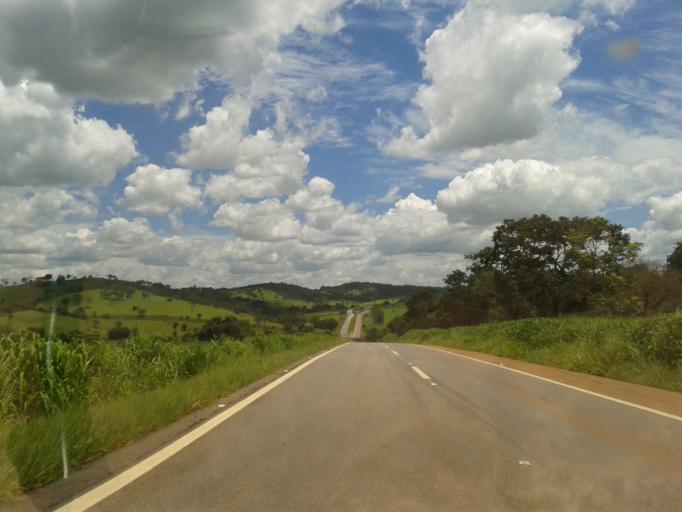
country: BR
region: Goias
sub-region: Neropolis
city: Neropolis
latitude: -16.2814
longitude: -49.2924
